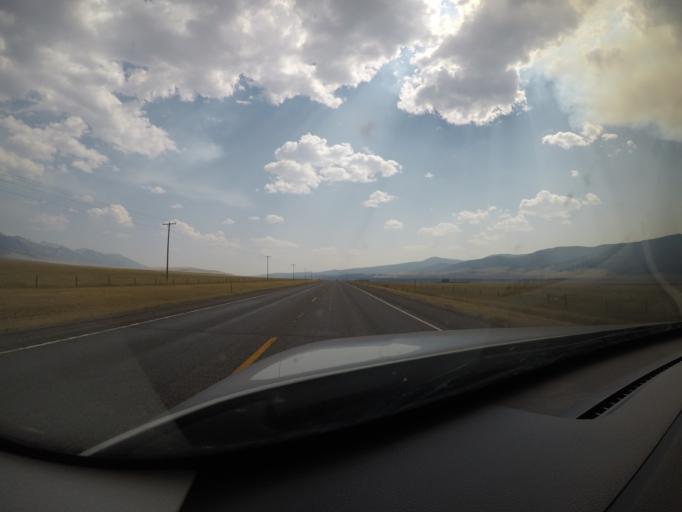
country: US
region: Montana
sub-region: Gallatin County
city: Big Sky
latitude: 45.0169
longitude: -111.6483
